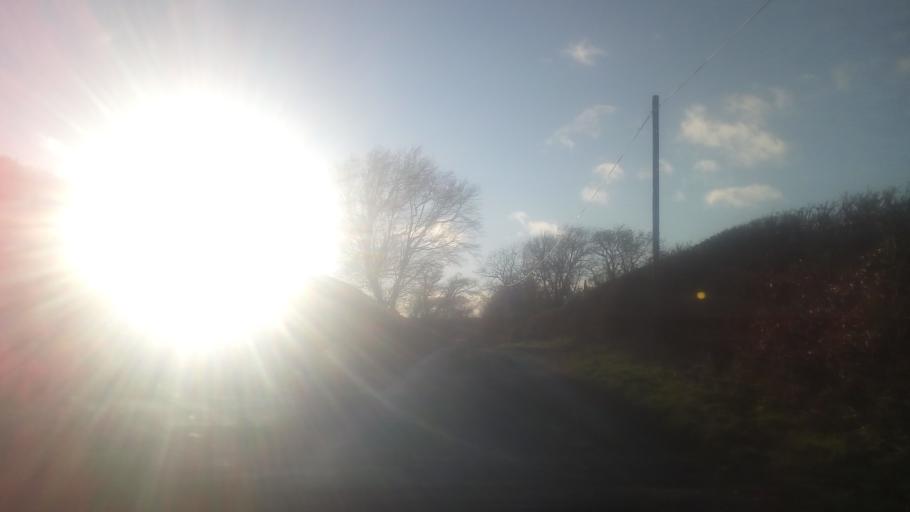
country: GB
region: Scotland
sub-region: The Scottish Borders
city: Jedburgh
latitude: 55.4703
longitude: -2.4708
